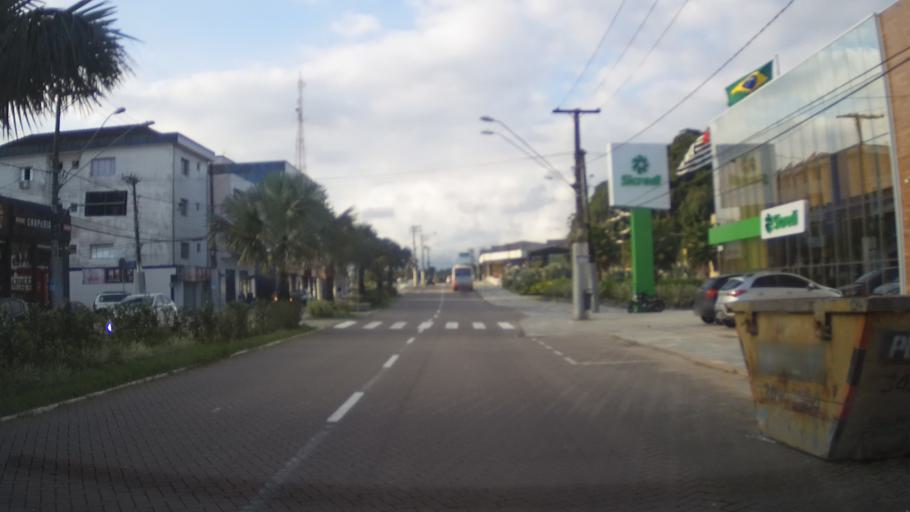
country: BR
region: Sao Paulo
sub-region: Praia Grande
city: Praia Grande
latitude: -24.0020
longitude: -46.4127
